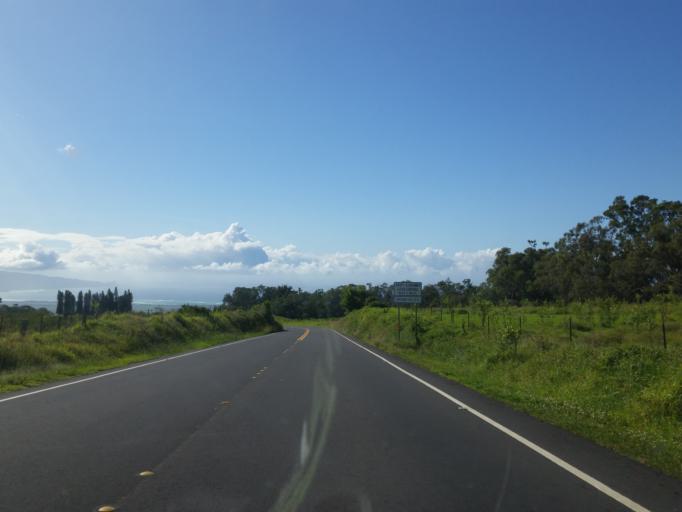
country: US
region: Hawaii
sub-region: Maui County
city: Pukalani
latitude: 20.8190
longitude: -156.3068
